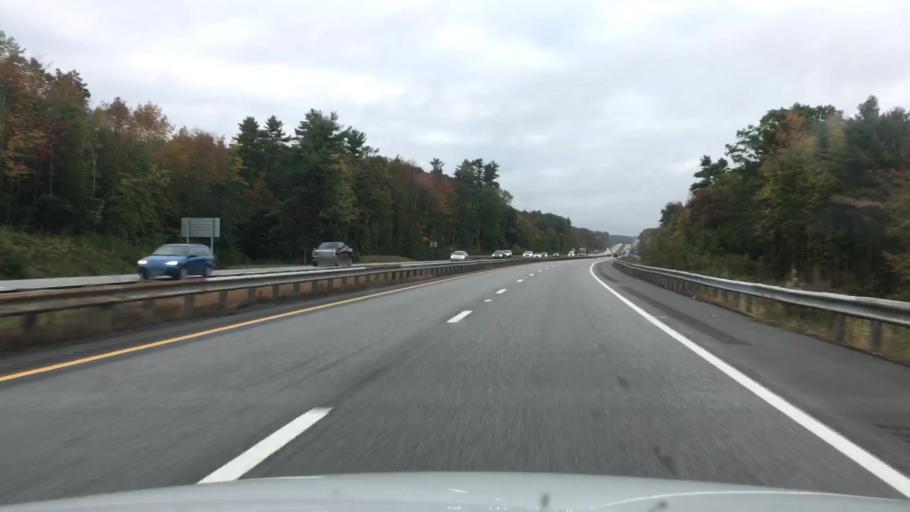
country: US
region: Maine
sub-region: Cumberland County
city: Cumberland Center
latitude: 43.7667
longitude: -70.3121
